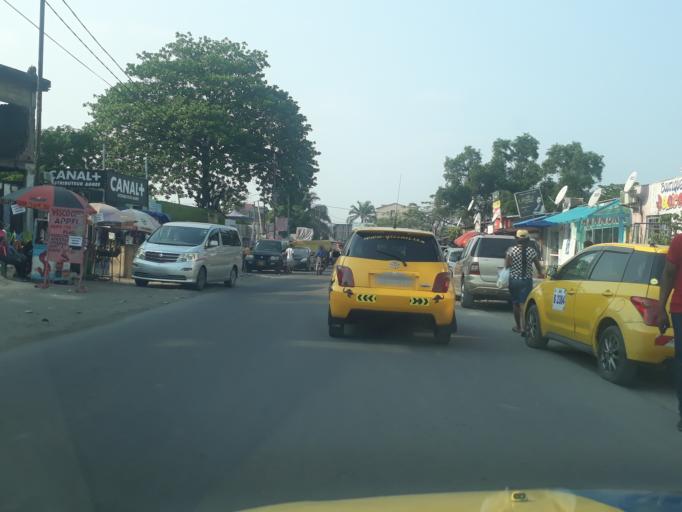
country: CD
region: Kinshasa
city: Kinshasa
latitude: -4.3206
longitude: 15.3295
